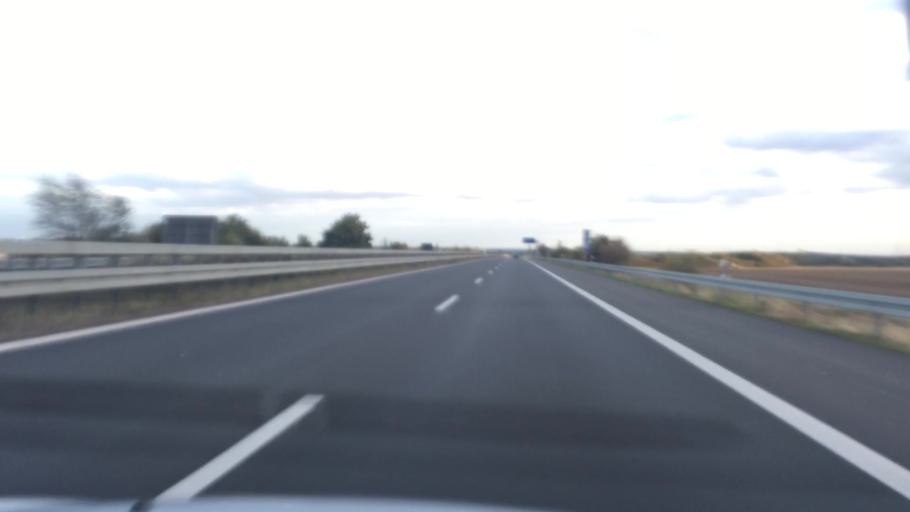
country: DE
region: Saxony-Anhalt
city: Oppin
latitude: 51.5479
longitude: 12.0099
